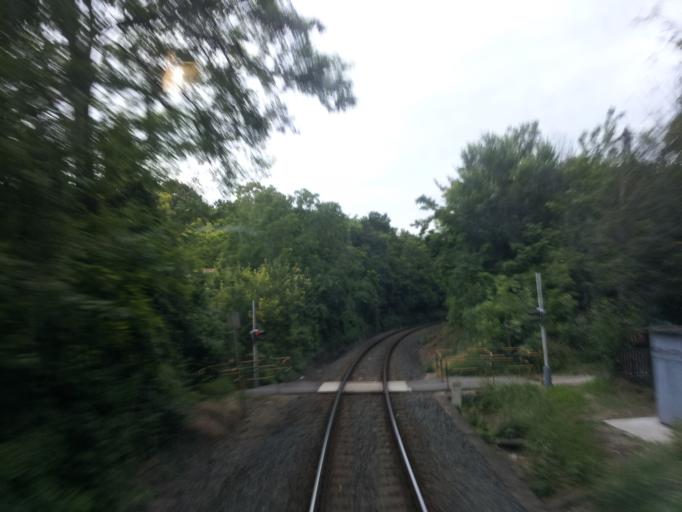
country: HU
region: Veszprem
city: Balatonkenese
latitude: 47.0146
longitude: 18.1611
